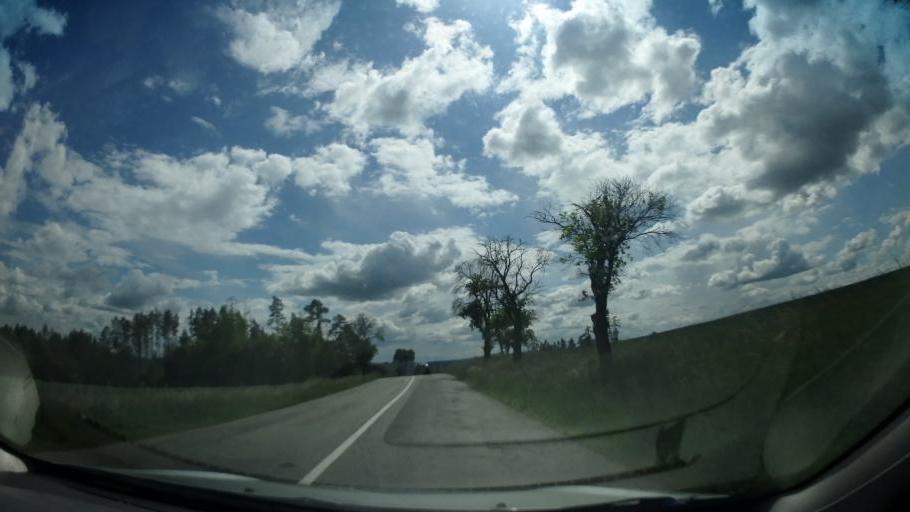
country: CZ
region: South Moravian
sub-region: Okres Blansko
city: Letovice
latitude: 49.5744
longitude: 16.5836
